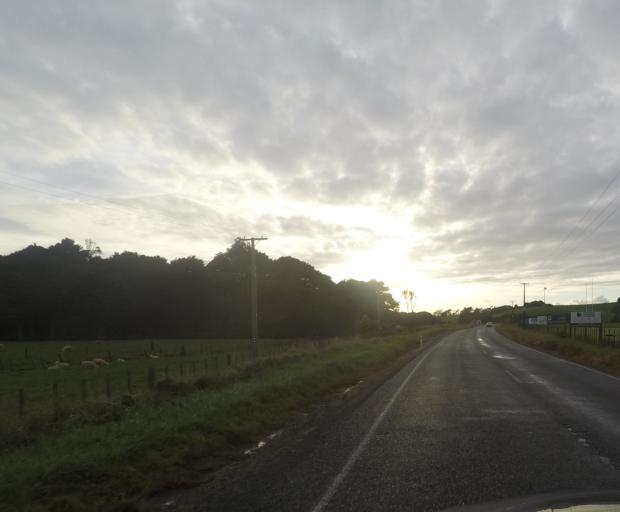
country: NZ
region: Auckland
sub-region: Auckland
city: Wellsford
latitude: -36.2201
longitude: 174.5794
